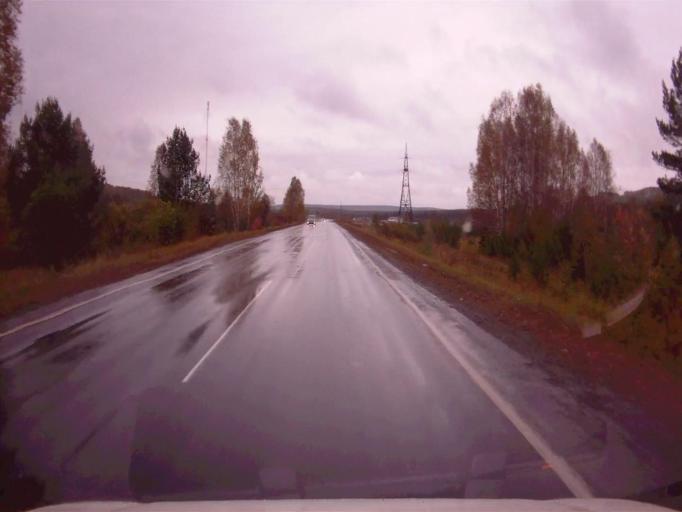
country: RU
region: Chelyabinsk
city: Verkhniy Ufaley
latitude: 55.9975
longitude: 60.3316
